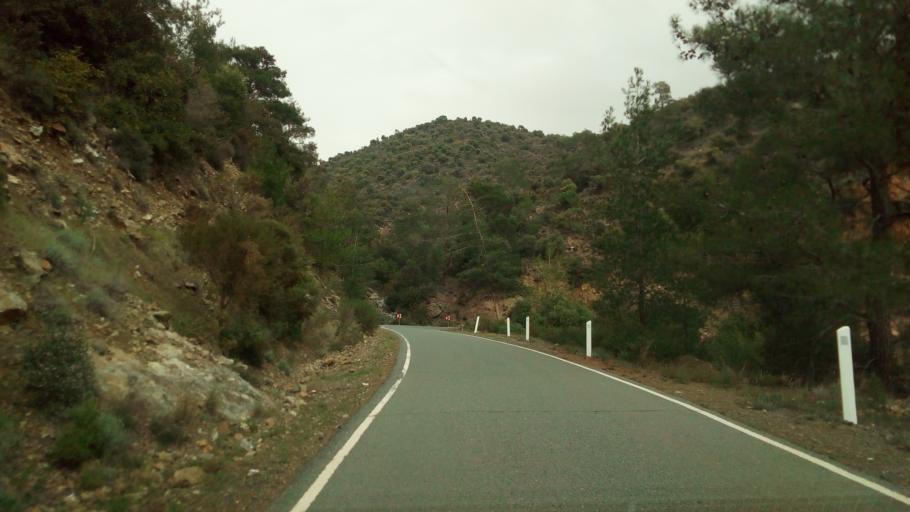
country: CY
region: Limassol
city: Mouttagiaka
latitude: 34.8077
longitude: 33.0856
